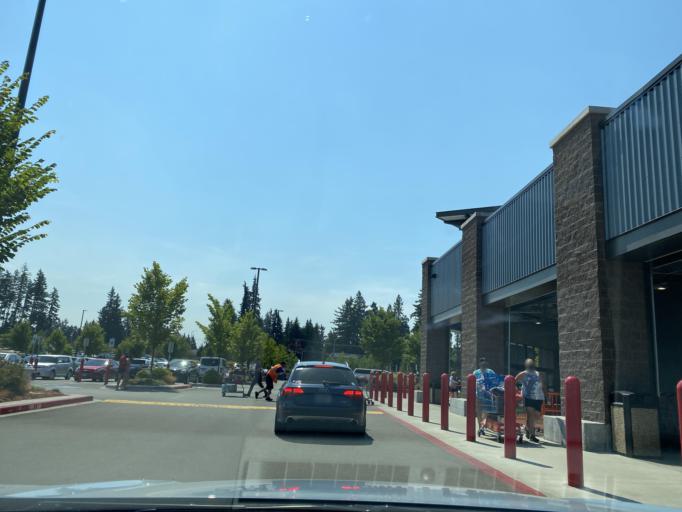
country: US
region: Washington
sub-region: Pierce County
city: Bonney Lake
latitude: 47.1669
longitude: -122.1586
